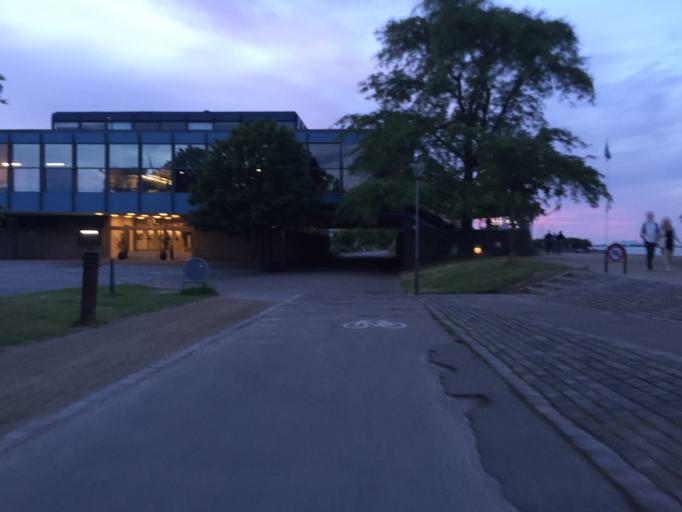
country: DK
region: Capital Region
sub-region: Kobenhavn
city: Christianshavn
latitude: 55.6909
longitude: 12.5986
